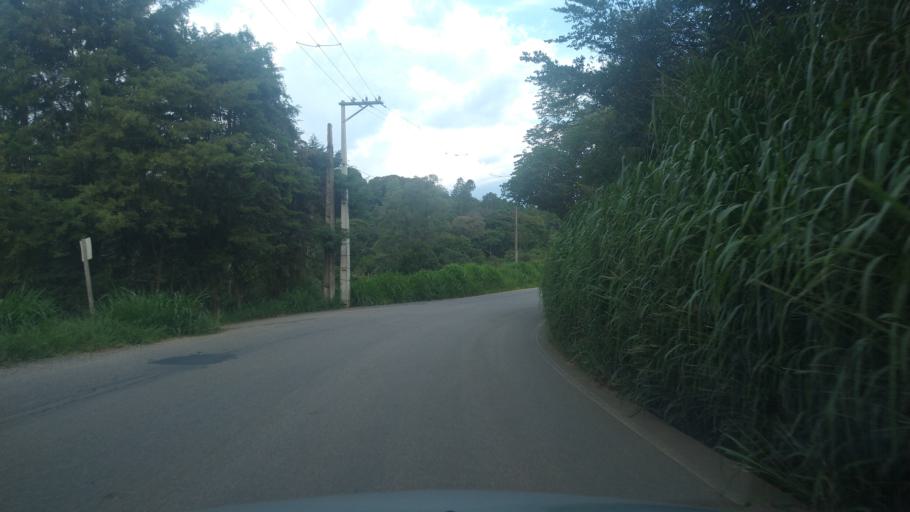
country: BR
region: Minas Gerais
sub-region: Extrema
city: Extrema
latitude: -22.8061
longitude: -46.3036
